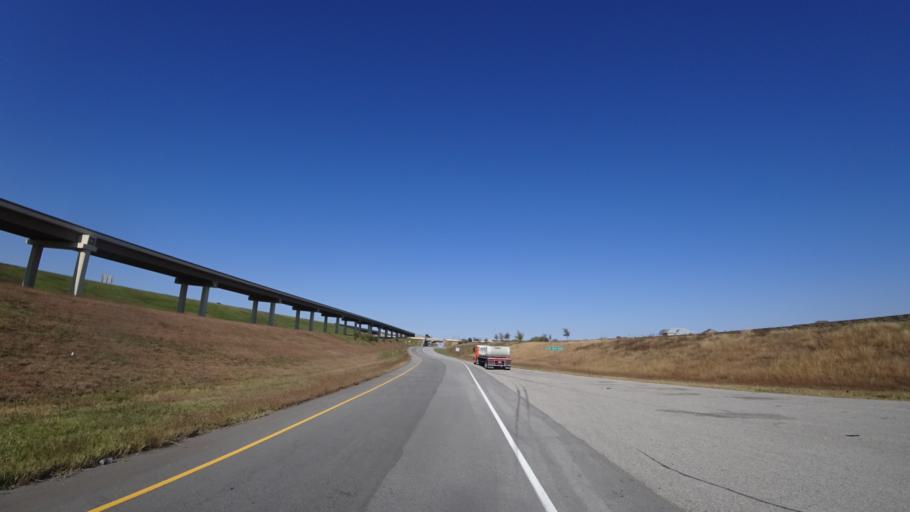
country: US
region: Texas
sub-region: Williamson County
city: Hutto
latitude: 30.5341
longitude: -97.5752
